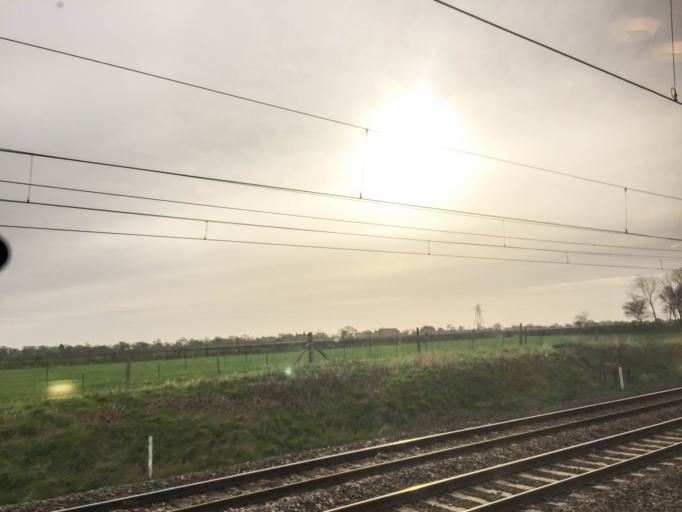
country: GB
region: England
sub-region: Cheshire East
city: Middlewich
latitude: 53.1669
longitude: -2.4773
